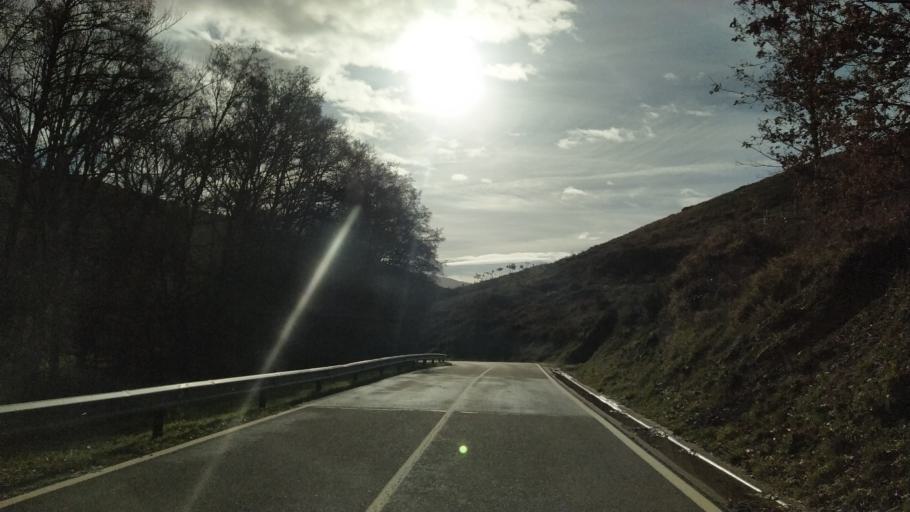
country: ES
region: Cantabria
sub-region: Provincia de Cantabria
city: San Martin de Elines
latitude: 42.8477
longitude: -3.9112
